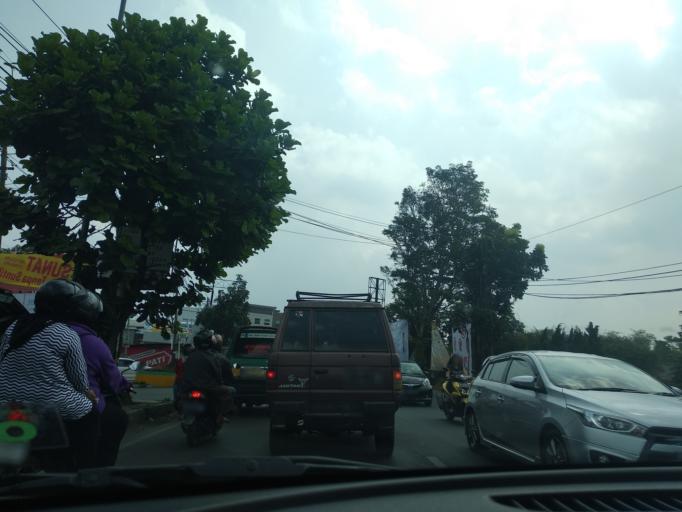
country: ID
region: West Java
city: Cimahi
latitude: -6.8687
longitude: 107.5266
